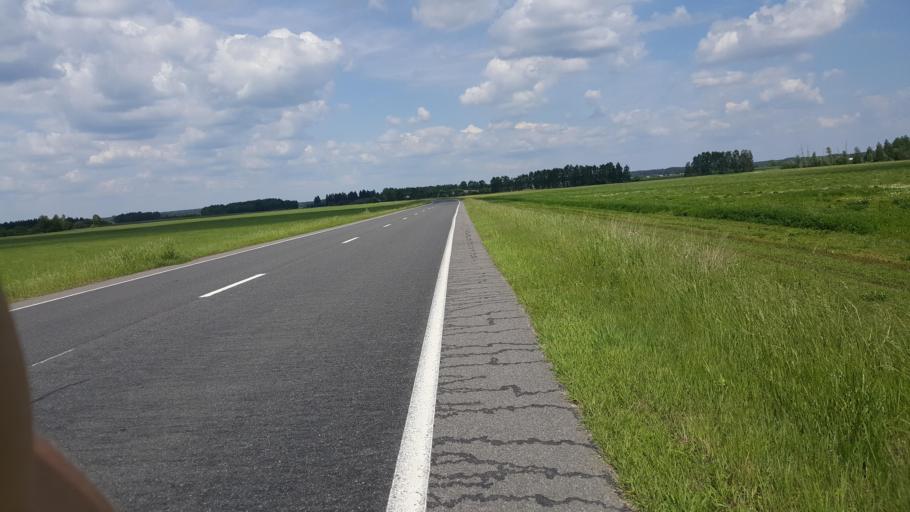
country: PL
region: Podlasie
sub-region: Powiat hajnowski
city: Bialowieza
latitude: 52.5554
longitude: 24.1364
